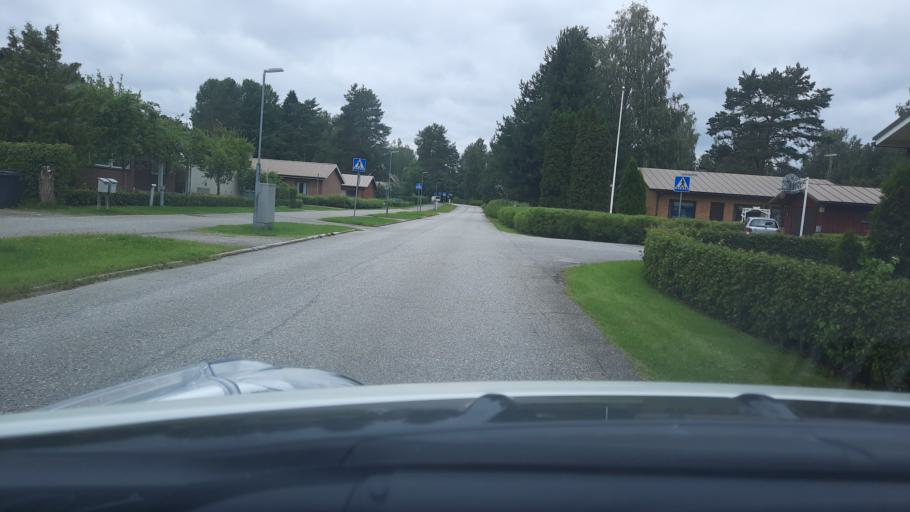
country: FI
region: North Karelia
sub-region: Joensuu
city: Joensuu
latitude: 62.6116
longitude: 29.8343
